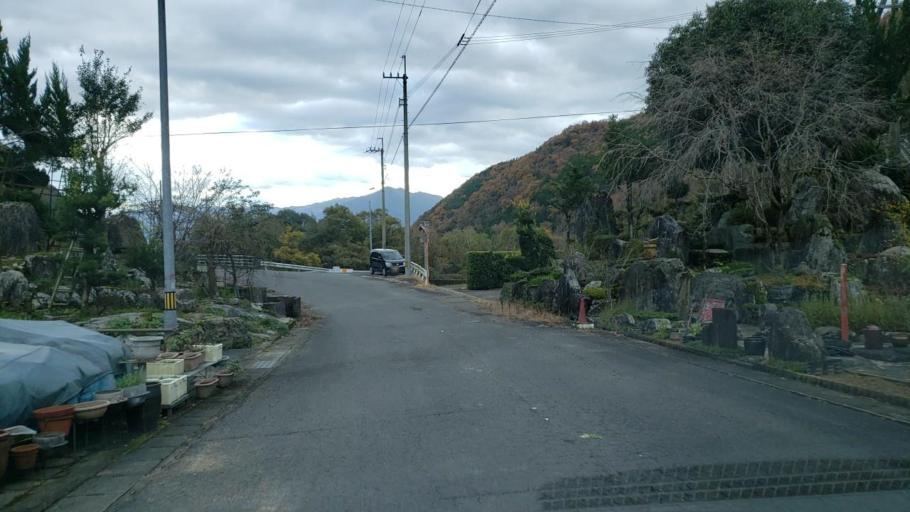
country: JP
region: Tokushima
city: Wakimachi
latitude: 34.1121
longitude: 134.2240
